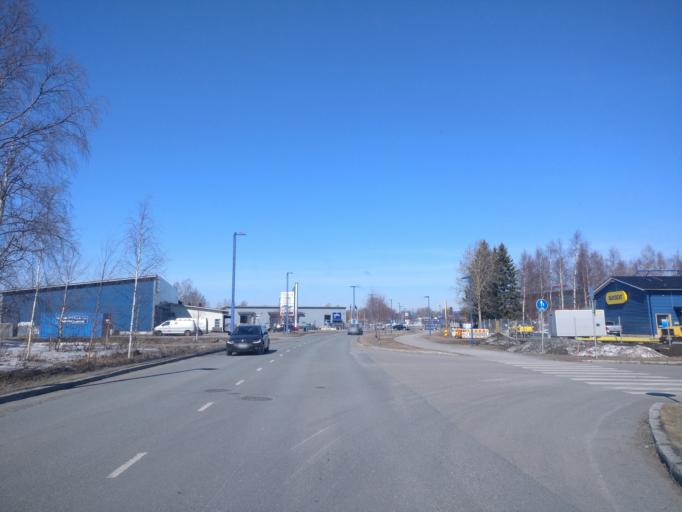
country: FI
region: Lapland
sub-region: Kemi-Tornio
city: Kemi
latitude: 65.7398
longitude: 24.5775
